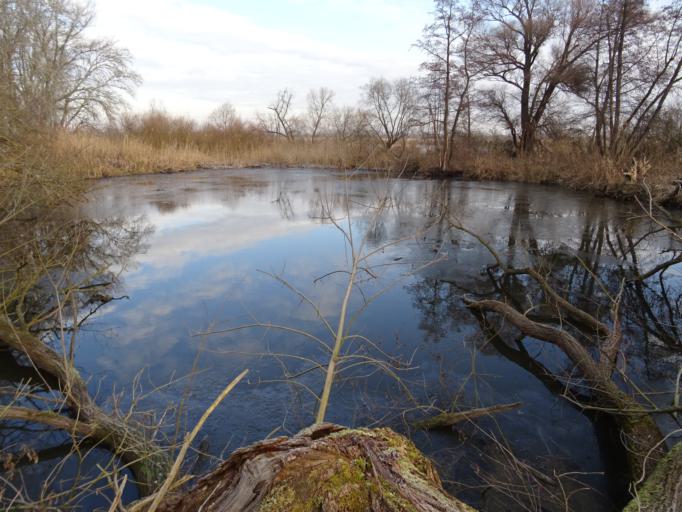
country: HU
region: Gyor-Moson-Sopron
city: Kony
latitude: 47.6096
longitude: 17.3548
